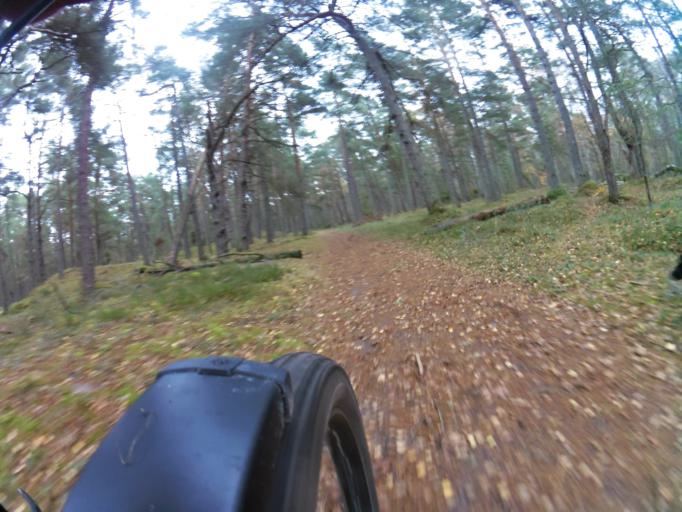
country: PL
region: Pomeranian Voivodeship
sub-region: Powiat leborski
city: Leba
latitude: 54.7757
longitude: 17.6739
